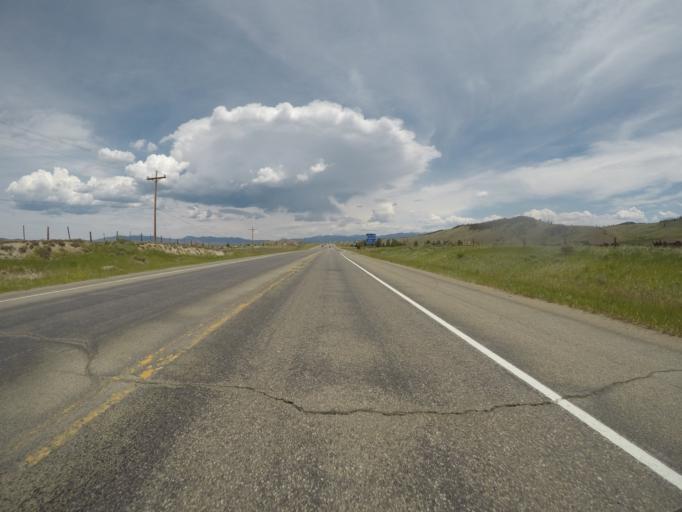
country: US
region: Colorado
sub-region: Grand County
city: Granby
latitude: 40.0584
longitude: -105.9286
